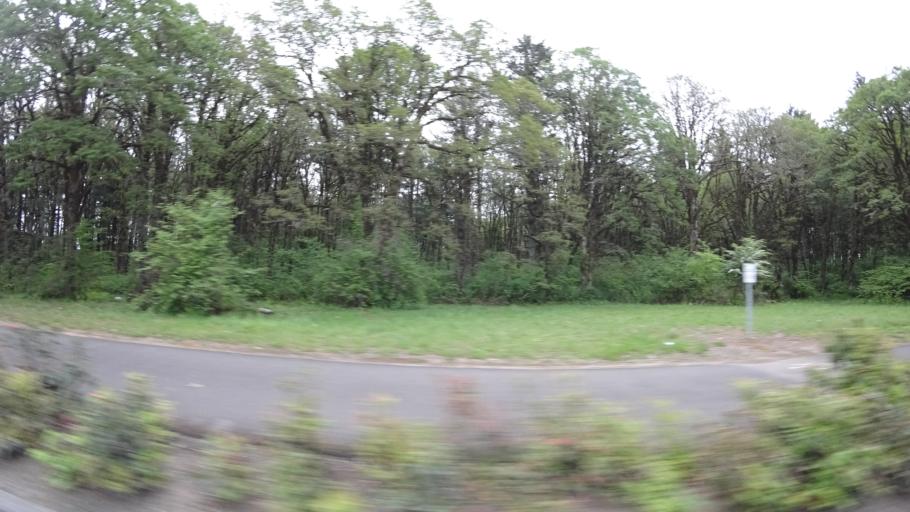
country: US
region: Oregon
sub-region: Washington County
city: Hillsboro
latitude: 45.5381
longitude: -122.9405
